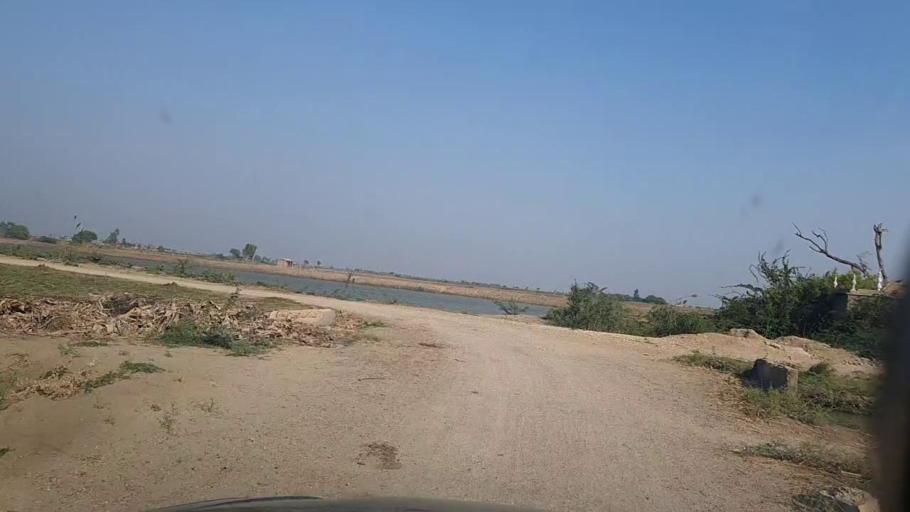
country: PK
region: Sindh
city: Thatta
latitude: 24.6084
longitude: 67.8761
